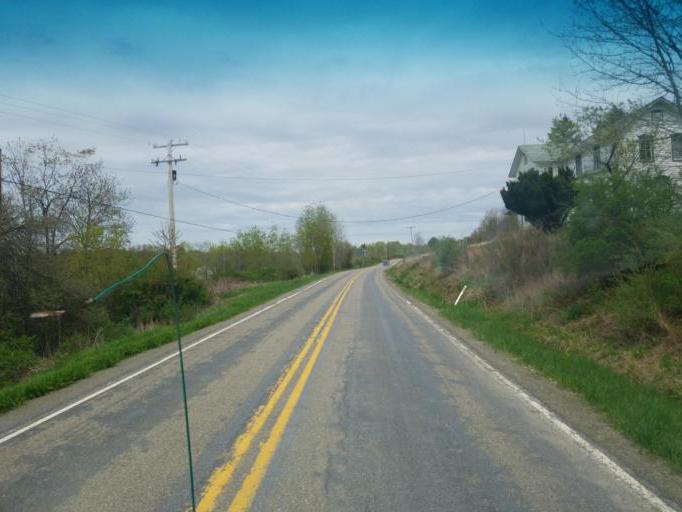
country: US
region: Pennsylvania
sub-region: Tioga County
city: Wellsboro
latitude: 41.6955
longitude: -77.4289
